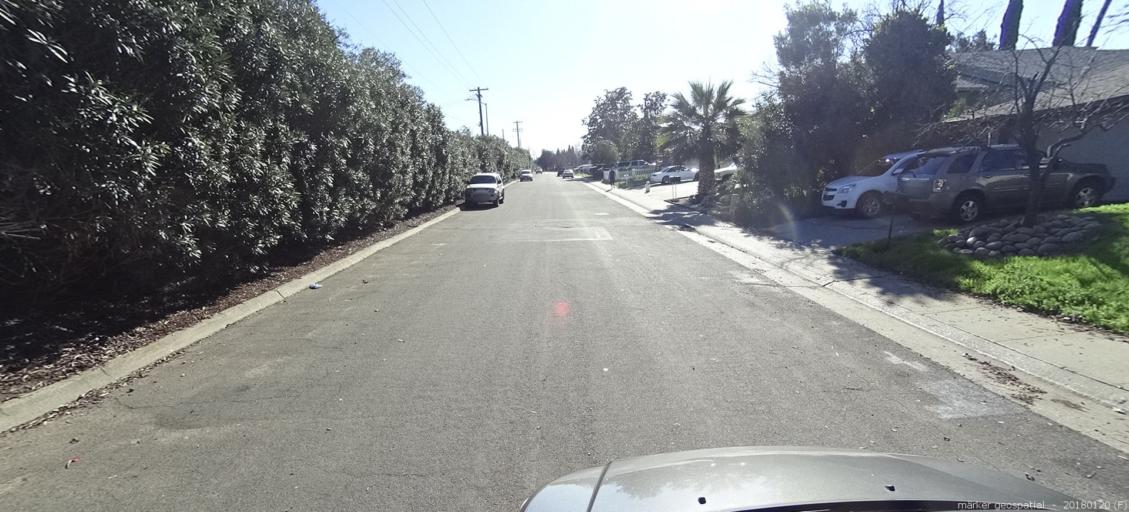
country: US
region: California
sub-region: Sacramento County
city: Rancho Cordova
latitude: 38.5702
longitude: -121.3182
